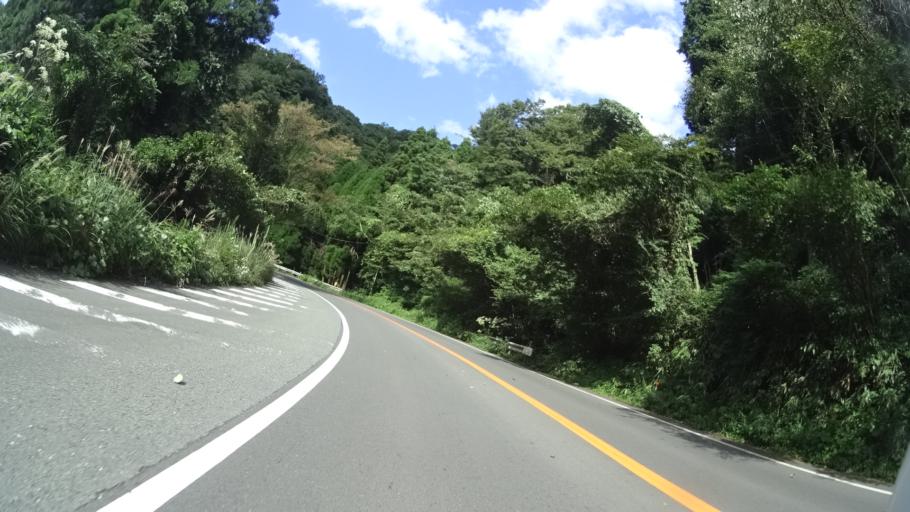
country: JP
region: Kumamoto
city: Aso
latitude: 32.8146
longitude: 131.1389
